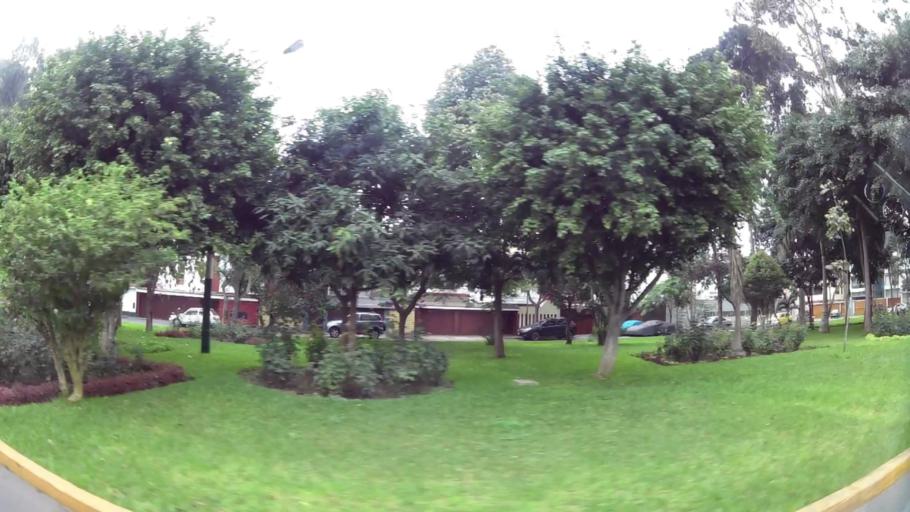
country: PE
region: Lima
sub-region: Lima
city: Surco
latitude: -12.1407
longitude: -76.9914
